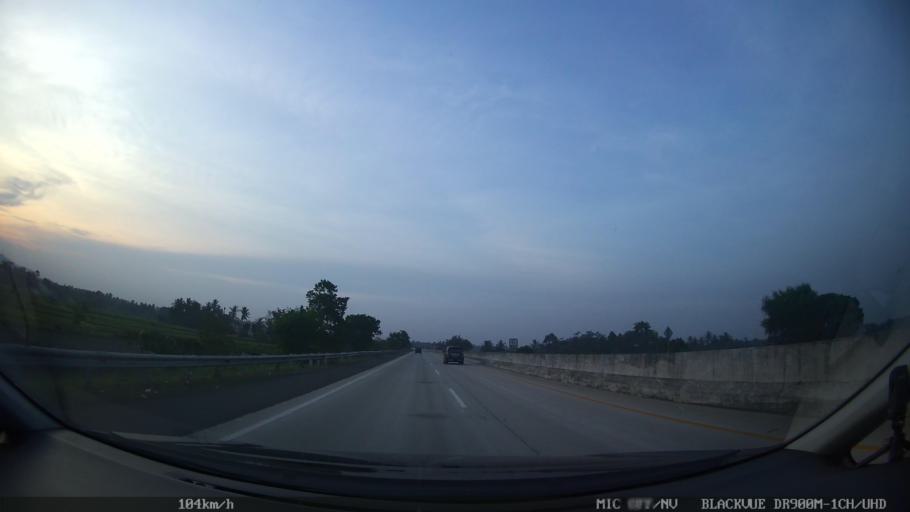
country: ID
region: Lampung
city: Penengahan
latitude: -5.7603
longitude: 105.7118
